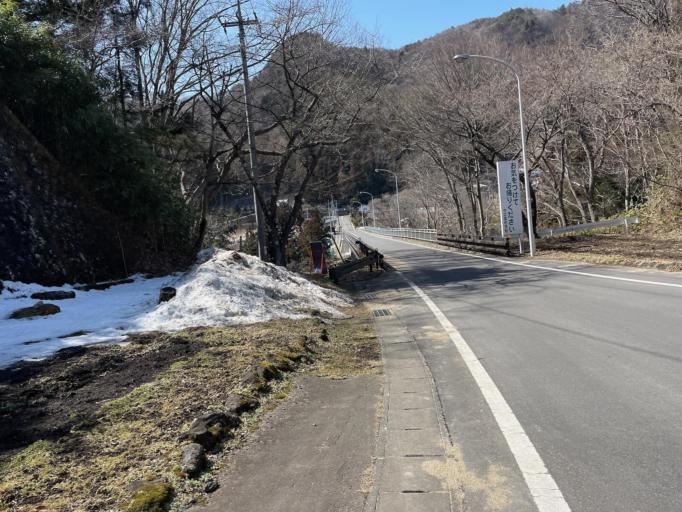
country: JP
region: Gunma
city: Nakanojomachi
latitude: 36.5779
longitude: 138.6261
